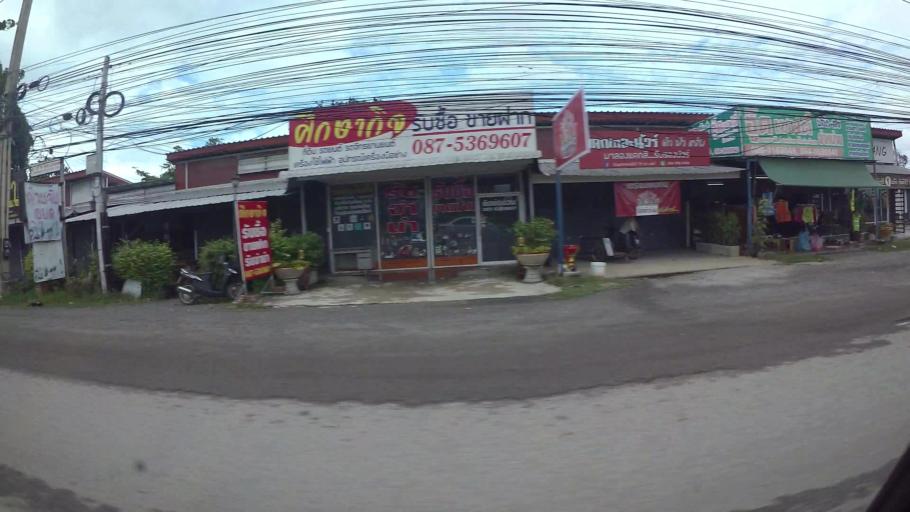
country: TH
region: Rayong
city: Rayong
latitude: 12.6962
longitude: 101.1970
